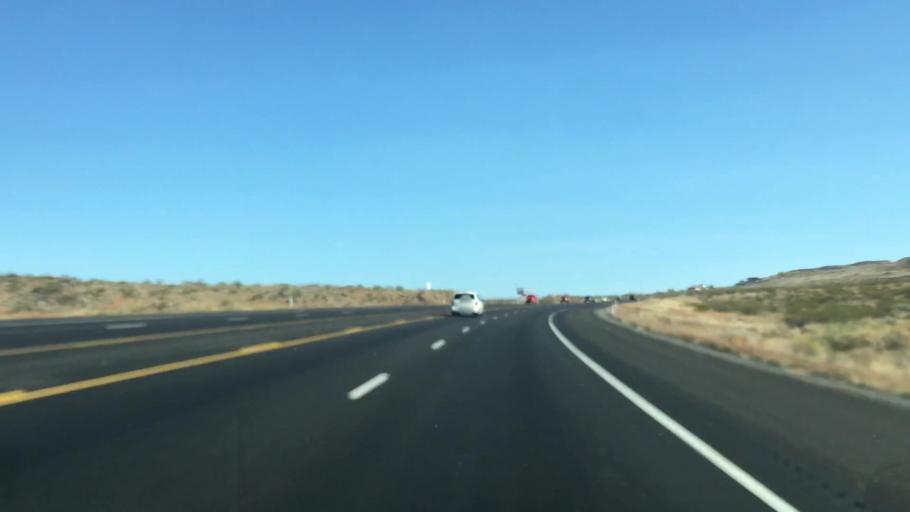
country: US
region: Utah
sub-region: Washington County
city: Hurricane
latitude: 37.1726
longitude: -113.3510
